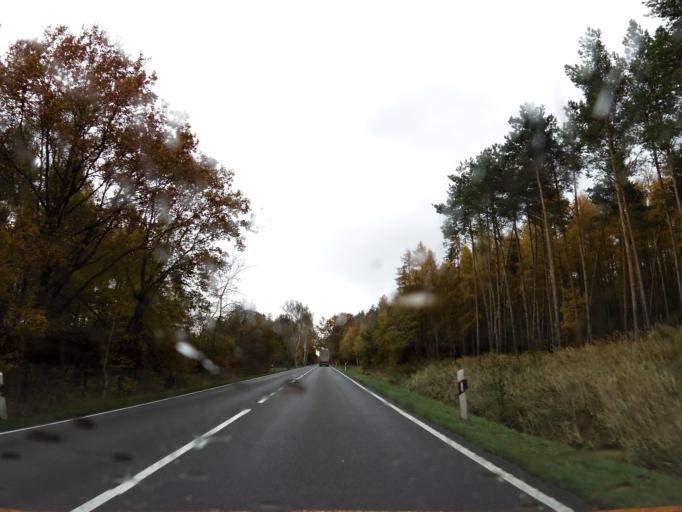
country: DE
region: Saxony-Anhalt
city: Kalbe
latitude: 52.6299
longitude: 11.3084
